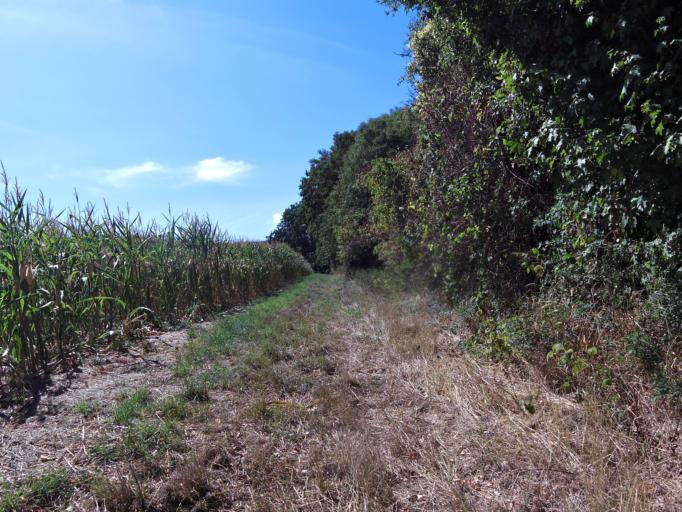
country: DE
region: Bavaria
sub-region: Regierungsbezirk Unterfranken
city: Theilheim
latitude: 49.7520
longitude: 10.0387
